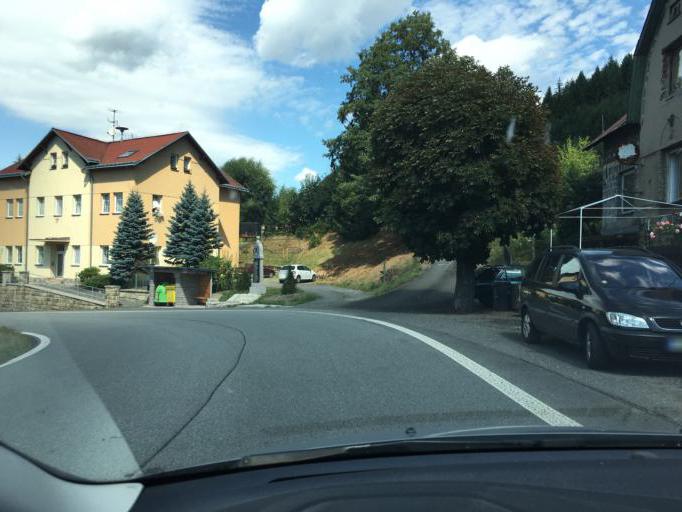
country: CZ
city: Plavy
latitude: 50.7018
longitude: 15.3282
